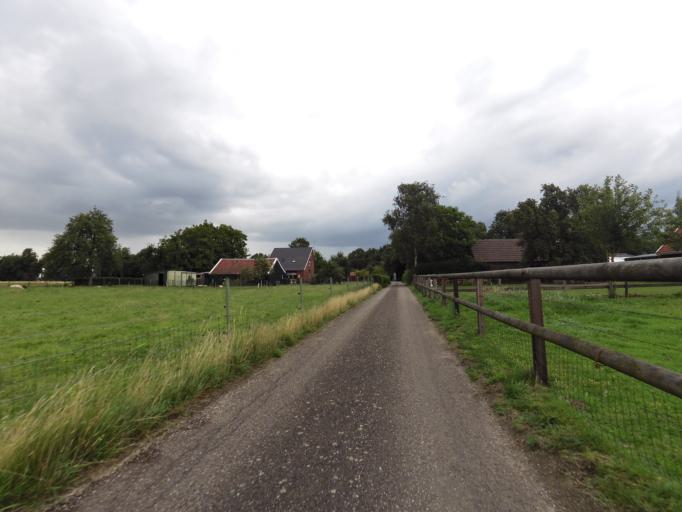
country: NL
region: Gelderland
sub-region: Gemeente Doesburg
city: Doesburg
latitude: 51.9656
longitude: 6.1997
